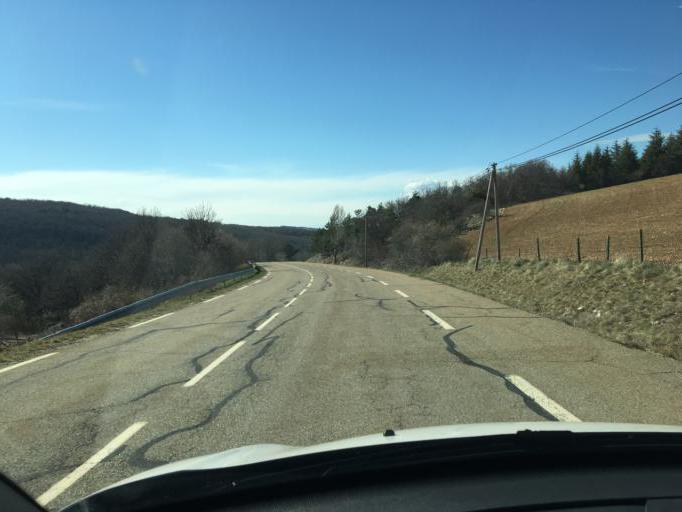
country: FR
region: Provence-Alpes-Cote d'Azur
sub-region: Departement du Vaucluse
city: Sault
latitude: 44.0061
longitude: 5.4804
